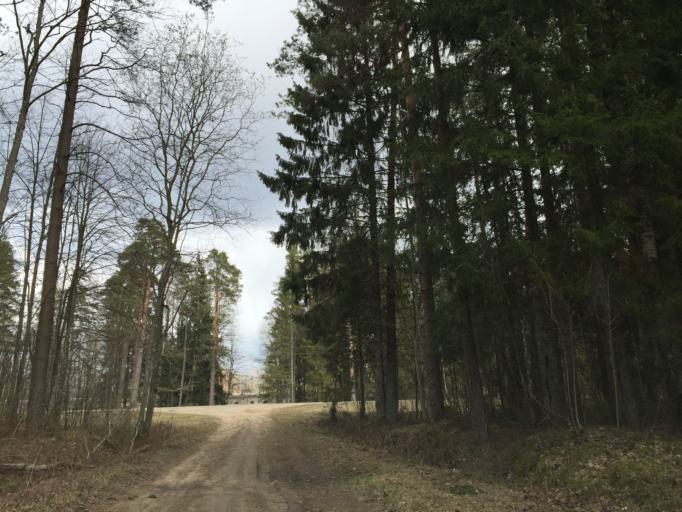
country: LV
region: Garkalne
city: Garkalne
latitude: 56.9664
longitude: 24.4878
